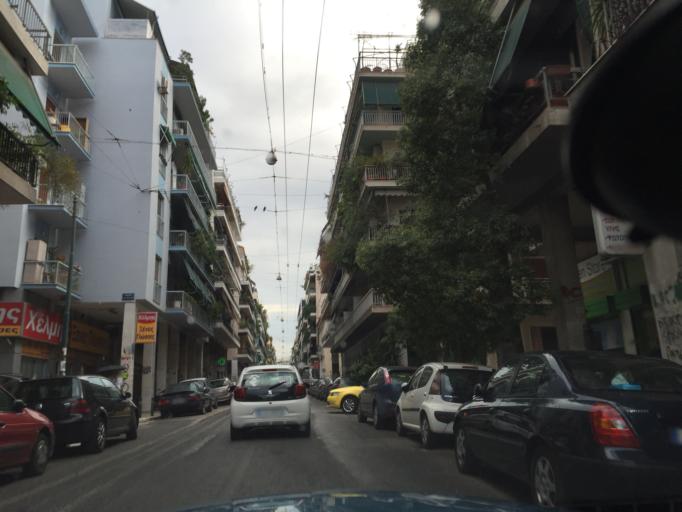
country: GR
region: Attica
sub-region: Nomarchia Athinas
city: Athens
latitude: 37.9645
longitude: 23.7240
